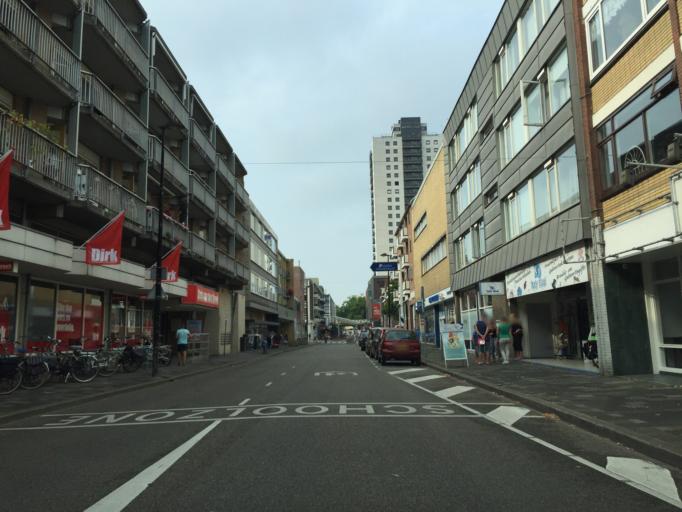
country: NL
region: South Holland
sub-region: Gemeente Vlaardingen
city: Vlaardingen
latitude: 51.9120
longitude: 4.3426
